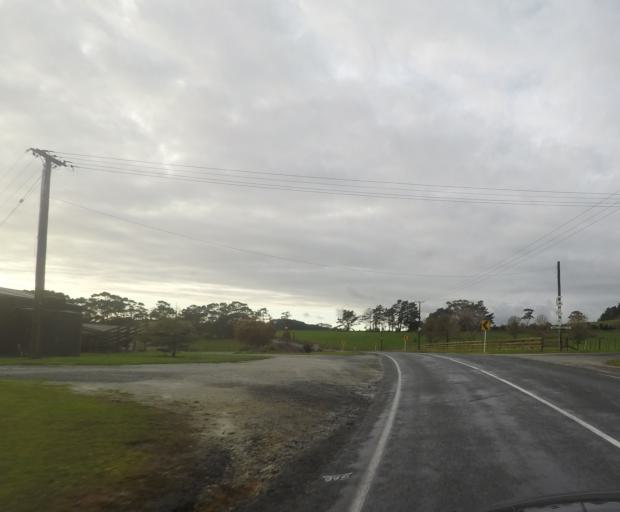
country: NZ
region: Auckland
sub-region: Auckland
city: Wellsford
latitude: -36.2223
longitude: 174.5720
